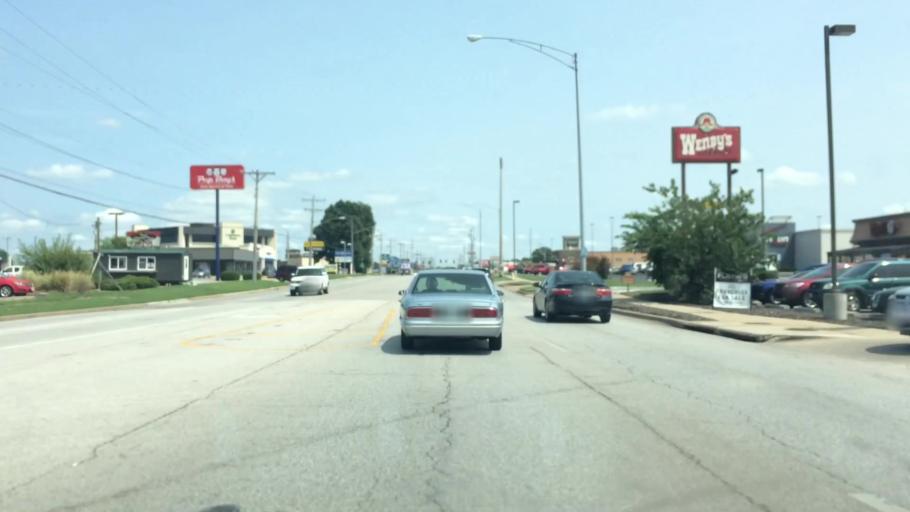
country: US
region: Missouri
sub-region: Greene County
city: Springfield
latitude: 37.1595
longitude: -93.2758
